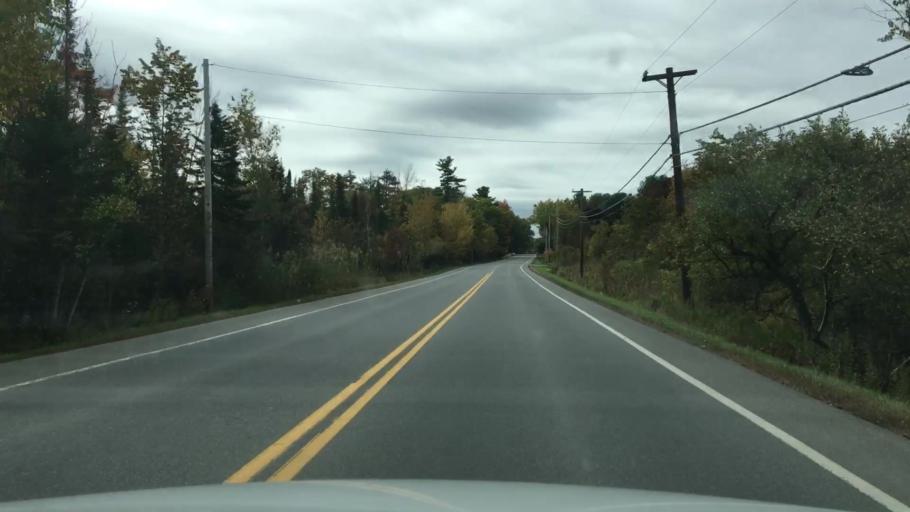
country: US
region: Maine
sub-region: Kennebec County
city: Waterville
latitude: 44.5569
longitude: -69.6704
